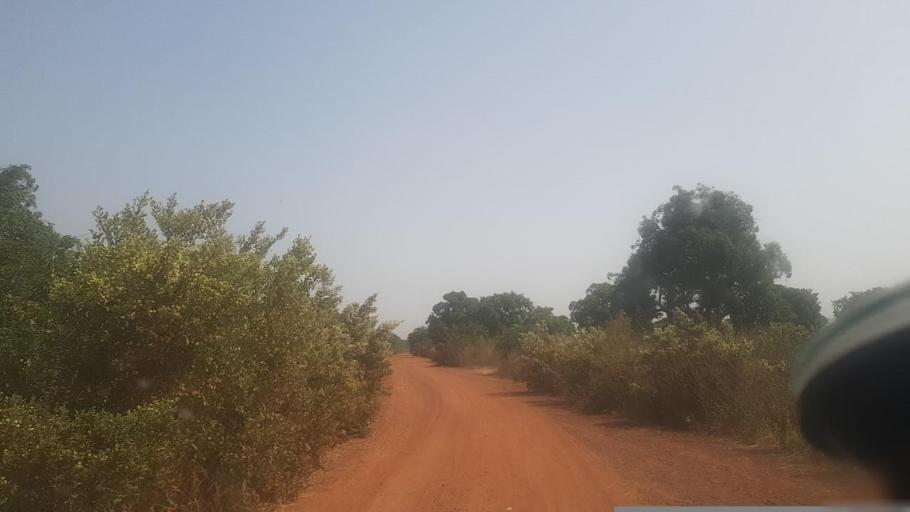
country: ML
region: Segou
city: Bla
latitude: 12.9226
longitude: -6.2634
